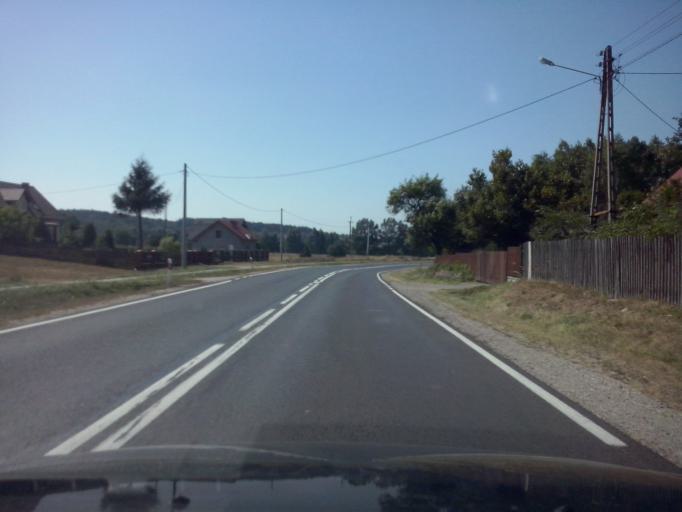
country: PL
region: Swietokrzyskie
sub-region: Powiat kielecki
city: Bieliny
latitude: 50.8191
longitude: 20.9152
